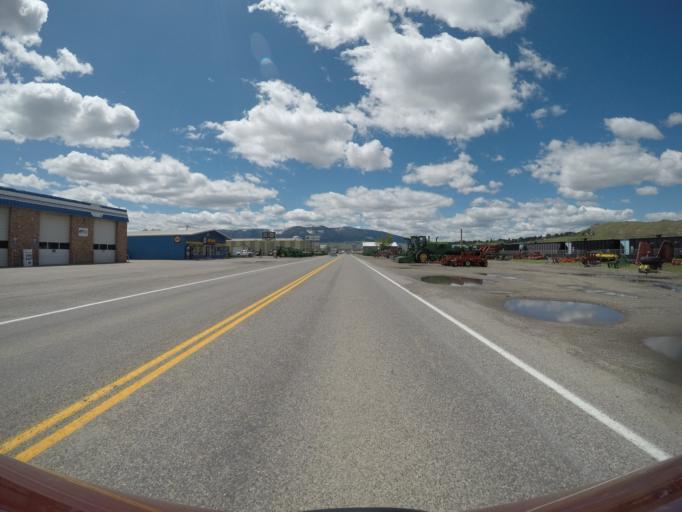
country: US
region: Montana
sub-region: Park County
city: Livingston
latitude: 45.6697
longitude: -110.5477
